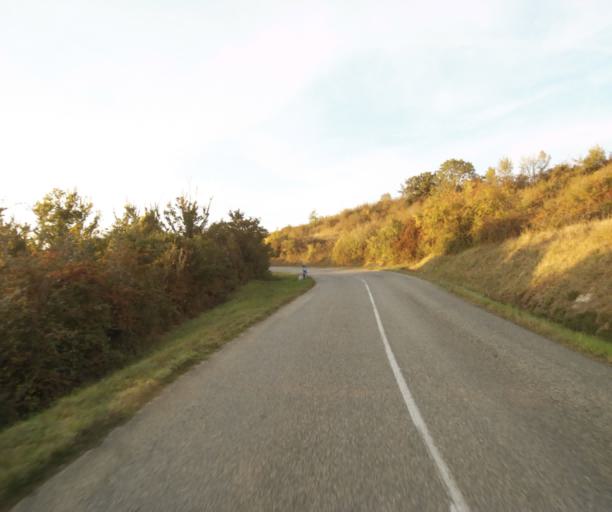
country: FR
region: Midi-Pyrenees
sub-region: Departement du Tarn-et-Garonne
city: Grisolles
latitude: 43.8315
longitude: 1.3078
